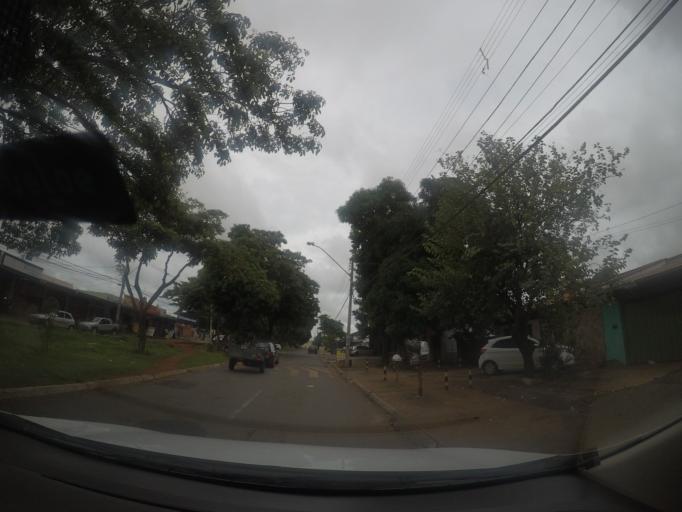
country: BR
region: Goias
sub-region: Trindade
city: Trindade
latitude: -16.6844
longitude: -49.3902
